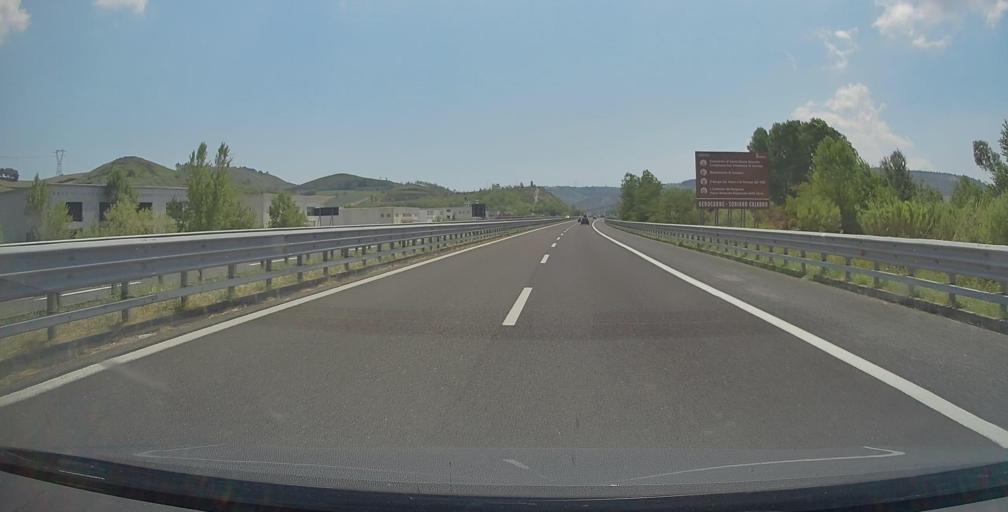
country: IT
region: Calabria
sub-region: Provincia di Vibo-Valentia
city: Soriano Calabro
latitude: 38.6351
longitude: 16.1734
